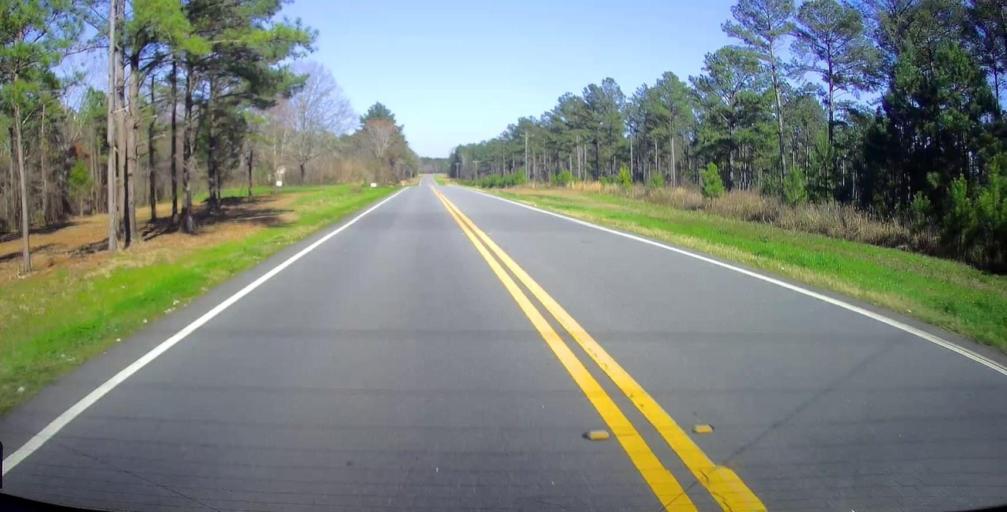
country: US
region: Georgia
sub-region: Dooly County
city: Unadilla
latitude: 32.3343
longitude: -83.8597
